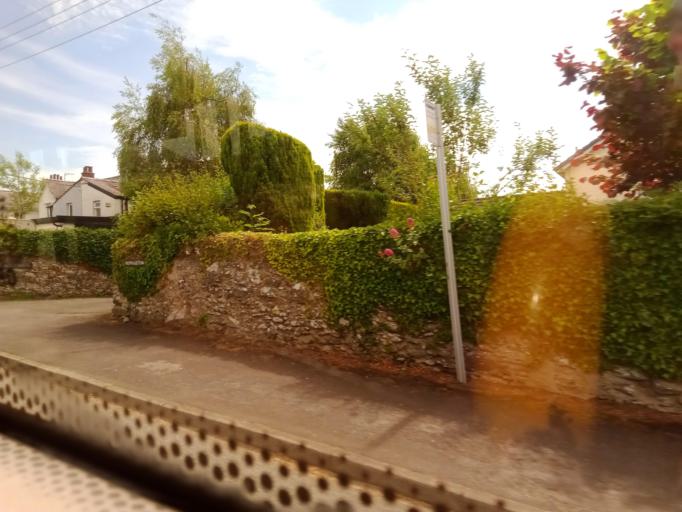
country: GB
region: Wales
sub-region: Anglesey
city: Menai Bridge
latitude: 53.2359
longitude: -4.1564
